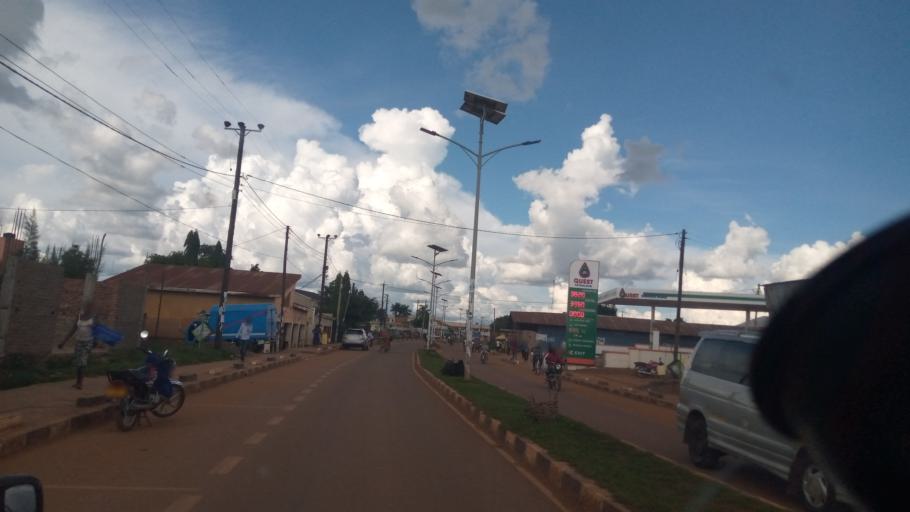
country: UG
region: Northern Region
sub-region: Lira District
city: Lira
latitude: 2.2421
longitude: 32.8915
